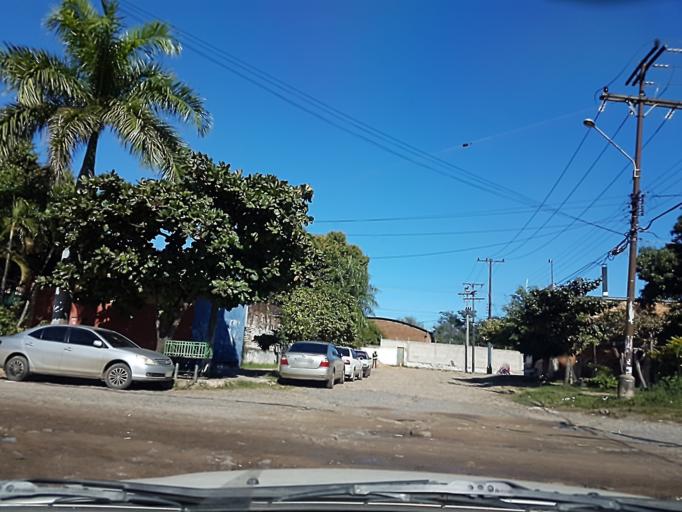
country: PY
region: Asuncion
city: Asuncion
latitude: -25.2537
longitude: -57.5824
